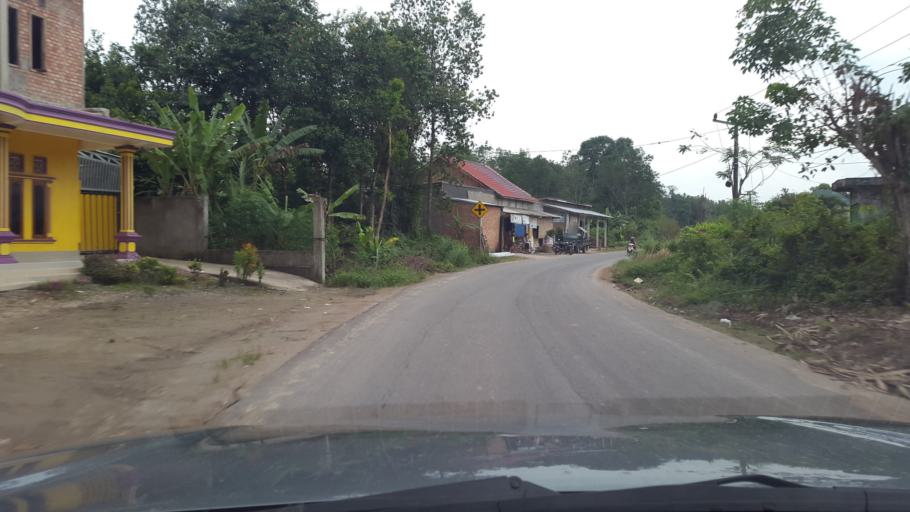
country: ID
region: South Sumatra
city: Gunungmenang
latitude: -3.2311
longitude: 104.0650
